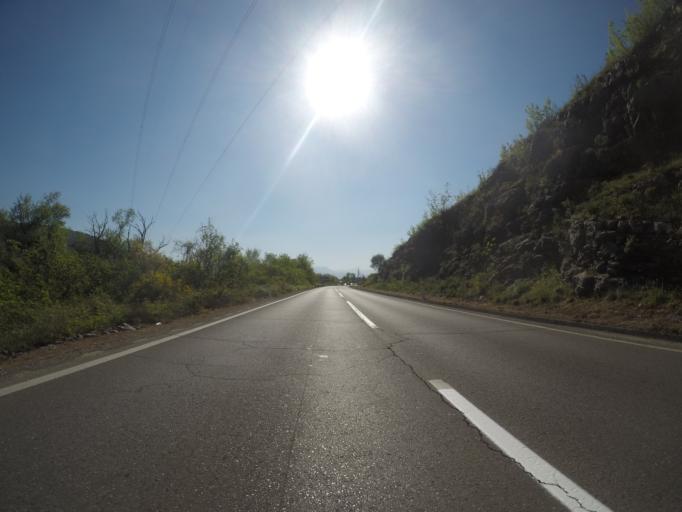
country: ME
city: Spuz
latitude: 42.4546
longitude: 19.1908
